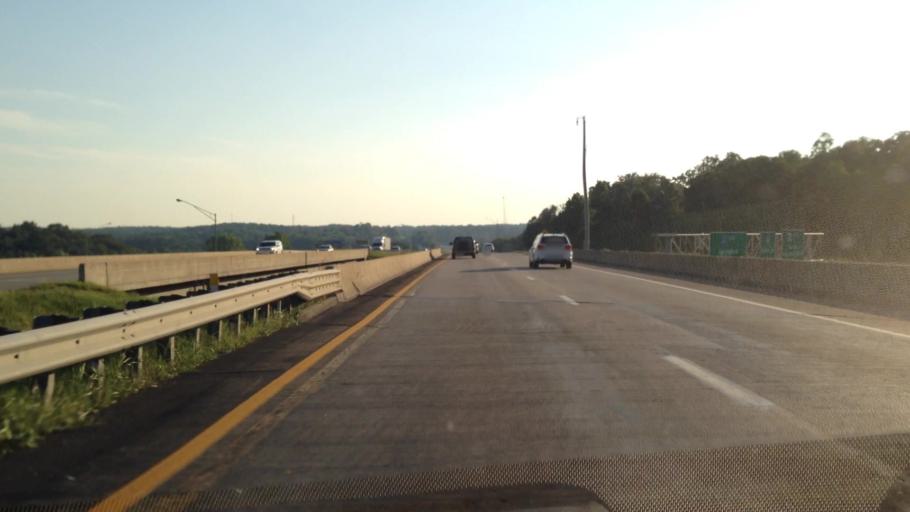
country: US
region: Missouri
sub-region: Jasper County
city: Joplin
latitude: 37.0368
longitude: -94.5142
